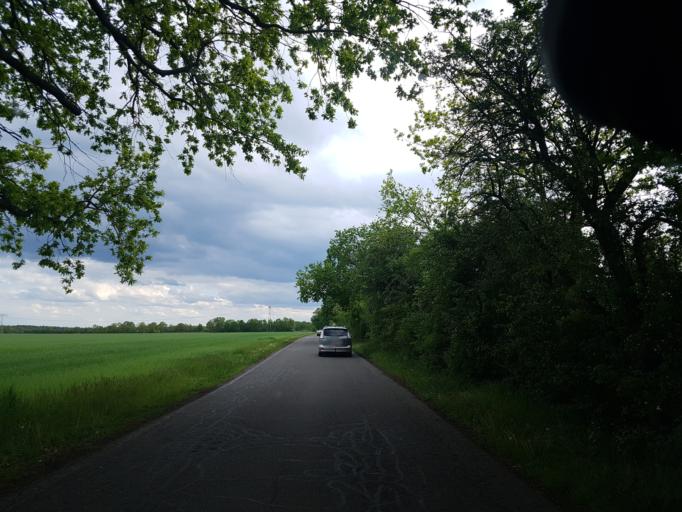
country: DE
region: Brandenburg
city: Grossraschen
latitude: 51.5818
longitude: 14.0624
